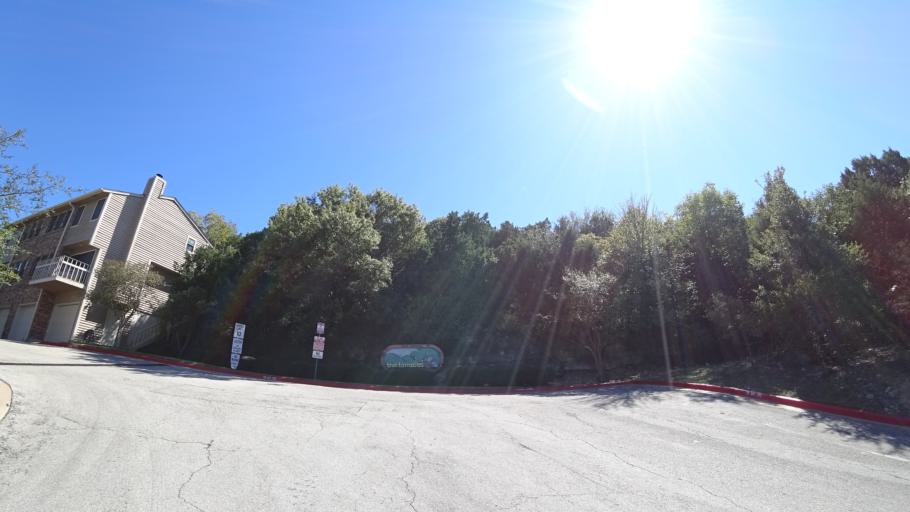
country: US
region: Texas
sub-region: Travis County
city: West Lake Hills
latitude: 30.3417
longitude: -97.7647
